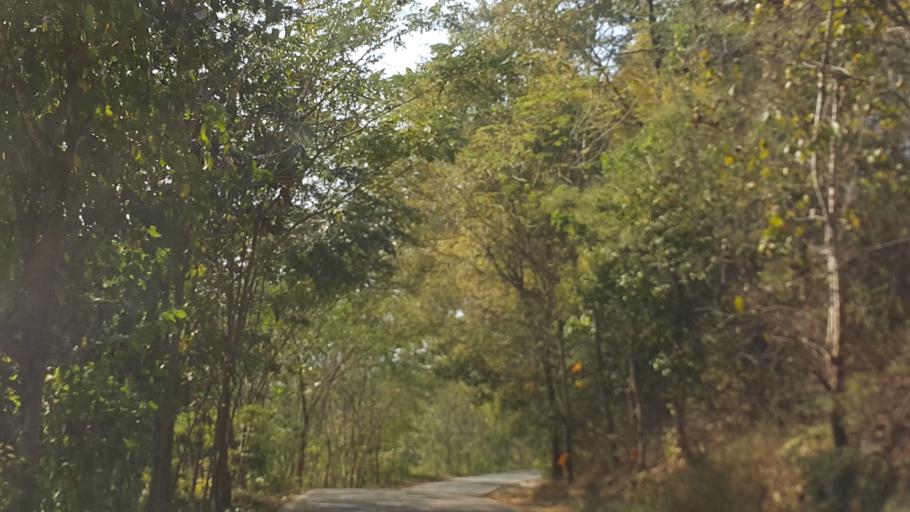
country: TH
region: Chiang Mai
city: Mae Taeng
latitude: 19.2162
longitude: 98.8625
